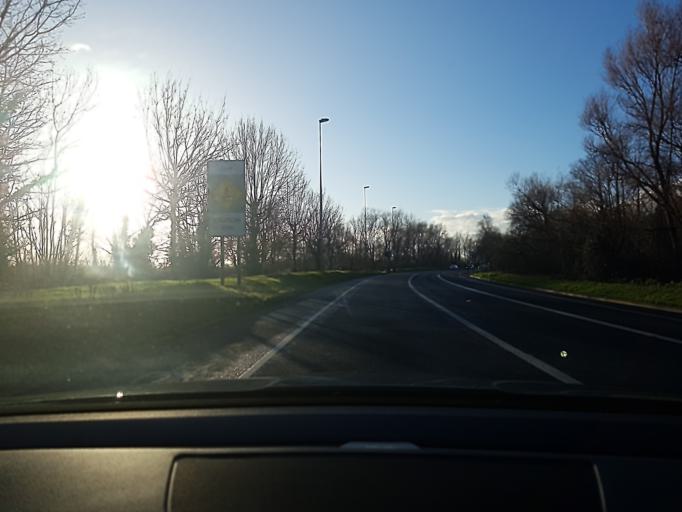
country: IE
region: Munster
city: Moyross
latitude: 52.6596
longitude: -8.6540
